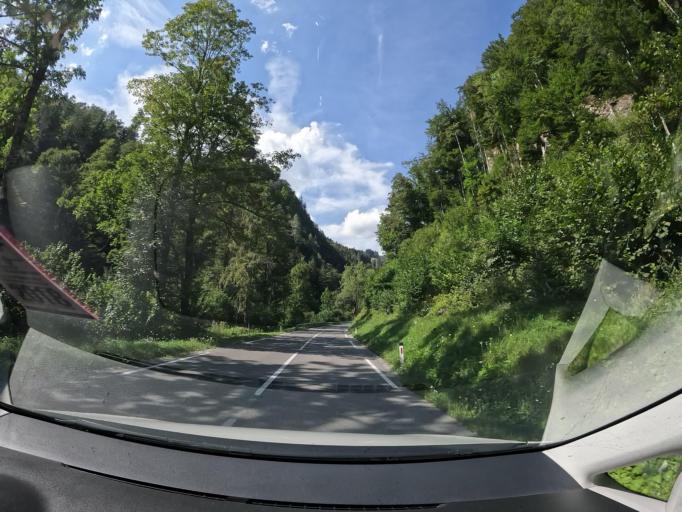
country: SI
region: Trzic
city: Trzic
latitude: 46.3954
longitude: 14.3439
